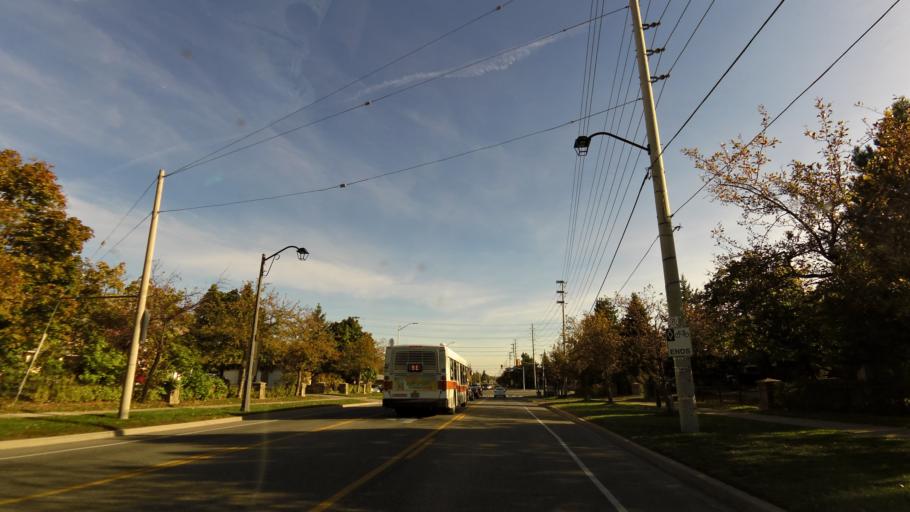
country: CA
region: Ontario
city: Mississauga
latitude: 43.5692
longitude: -79.6969
